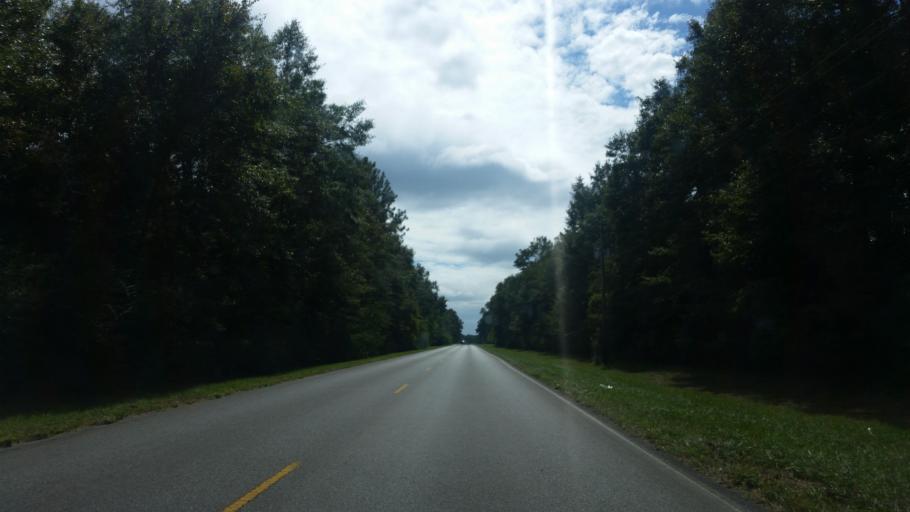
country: US
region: Florida
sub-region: Santa Rosa County
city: Point Baker
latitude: 30.7597
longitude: -86.9428
